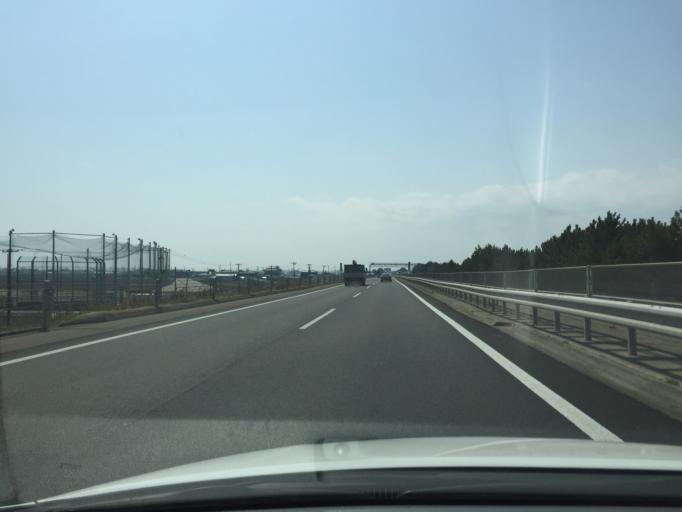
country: JP
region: Miyagi
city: Sendai-shi
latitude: 38.2277
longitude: 140.9529
